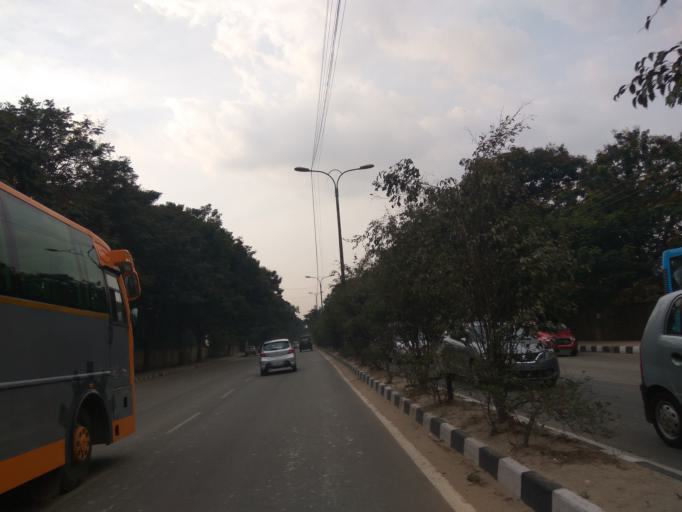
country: IN
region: Karnataka
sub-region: Bangalore Urban
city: Bangalore
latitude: 12.9737
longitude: 77.7112
